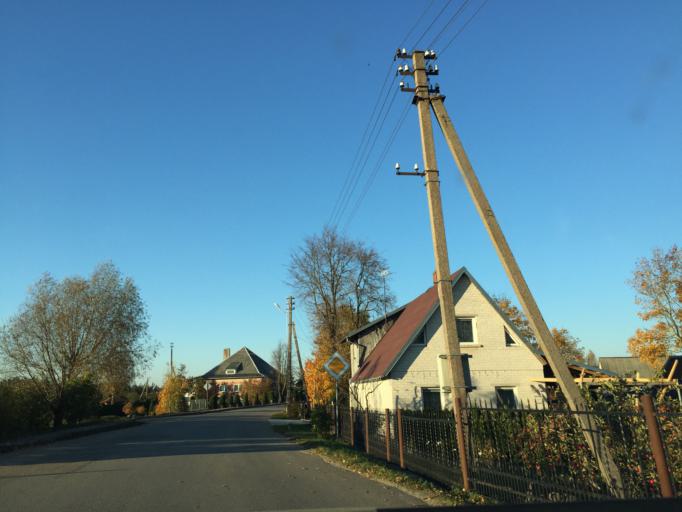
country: LT
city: Vieksniai
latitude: 56.2441
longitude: 22.5190
